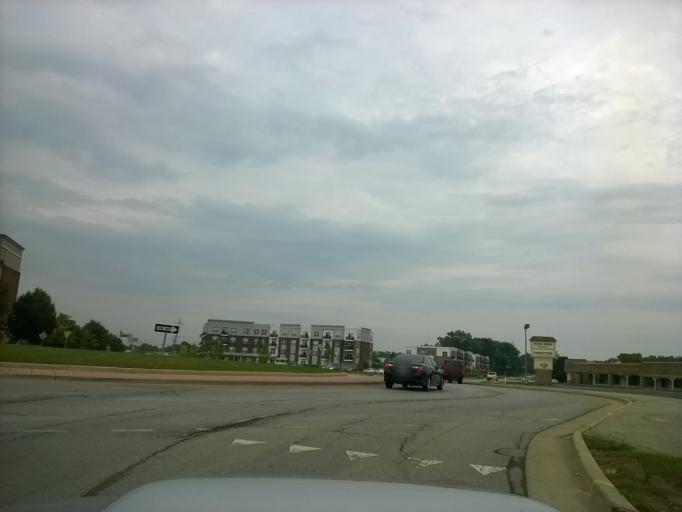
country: US
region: Indiana
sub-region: Hamilton County
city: Carmel
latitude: 39.9676
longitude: -86.1552
